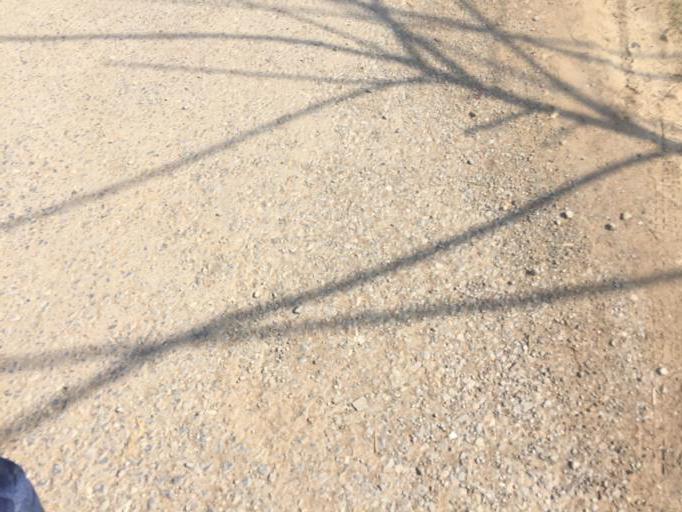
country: LA
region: Phongsali
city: Phongsali
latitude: 21.6664
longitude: 102.0891
